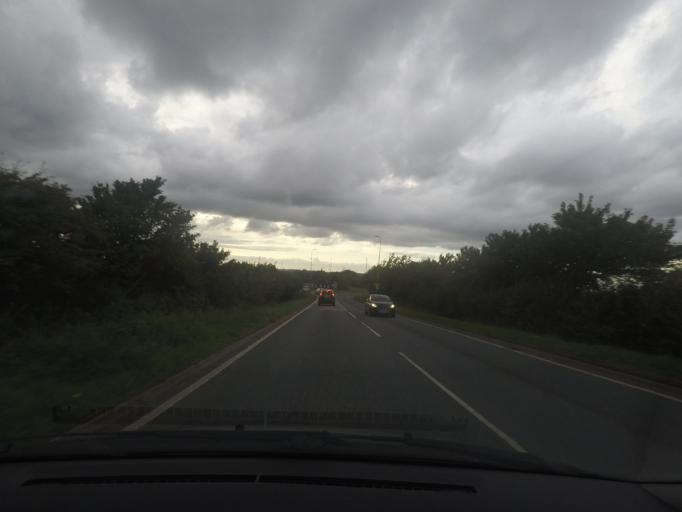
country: GB
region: England
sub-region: Lincolnshire
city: Louth
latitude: 53.3434
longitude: 0.0052
